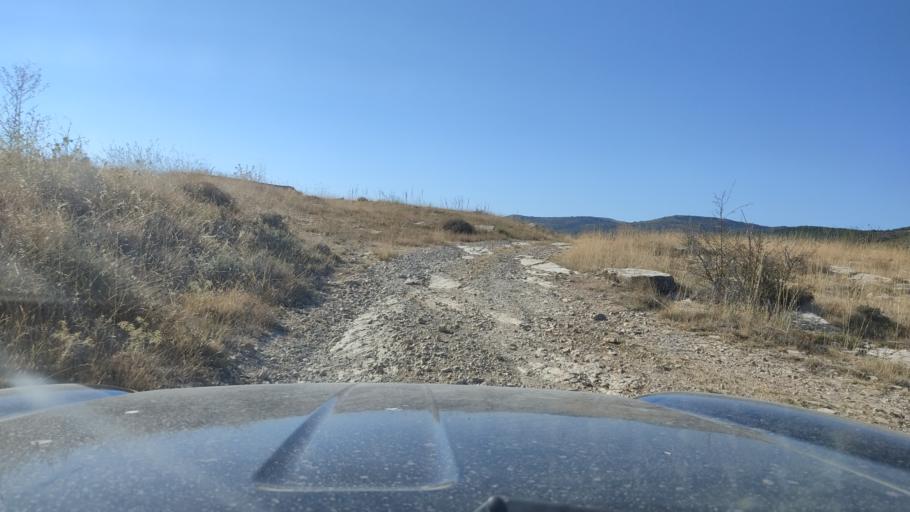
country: ES
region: Aragon
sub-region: Provincia de Teruel
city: Monforte de Moyuela
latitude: 41.0330
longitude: -1.0140
